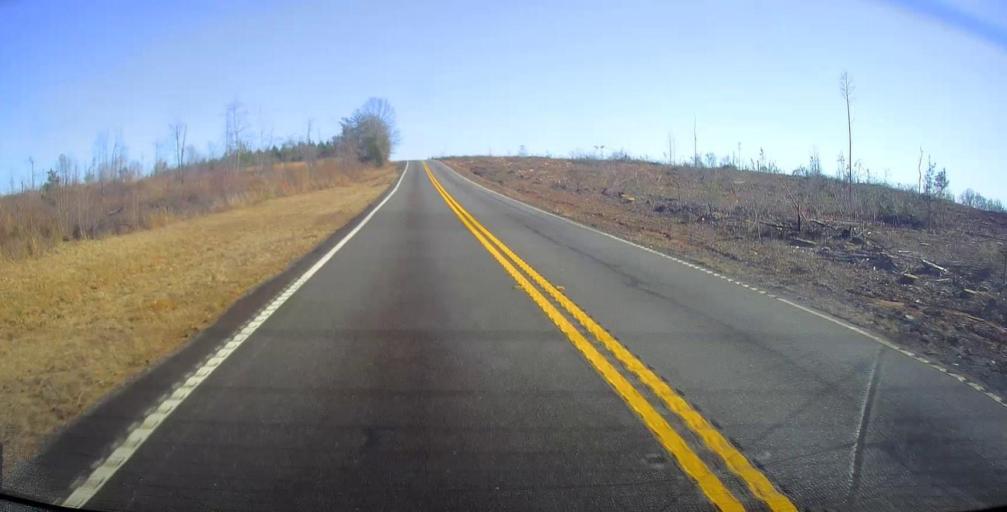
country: US
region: Georgia
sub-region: Talbot County
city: Talbotton
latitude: 32.6662
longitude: -84.4644
